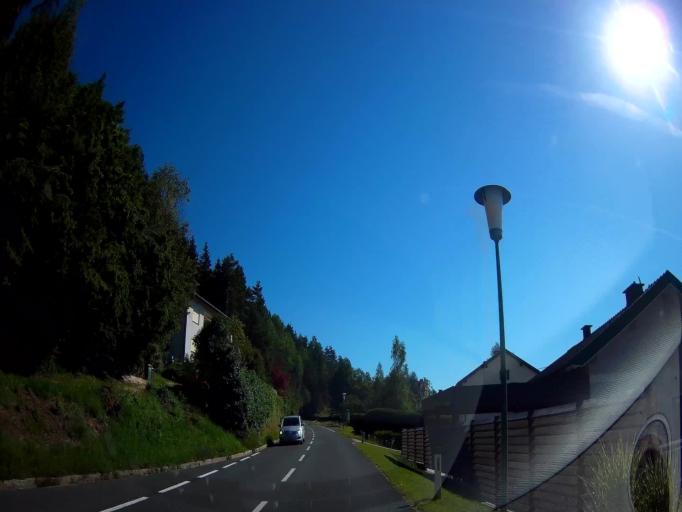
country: AT
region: Carinthia
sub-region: Politischer Bezirk Klagenfurt Land
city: Grafenstein
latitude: 46.6372
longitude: 14.5474
